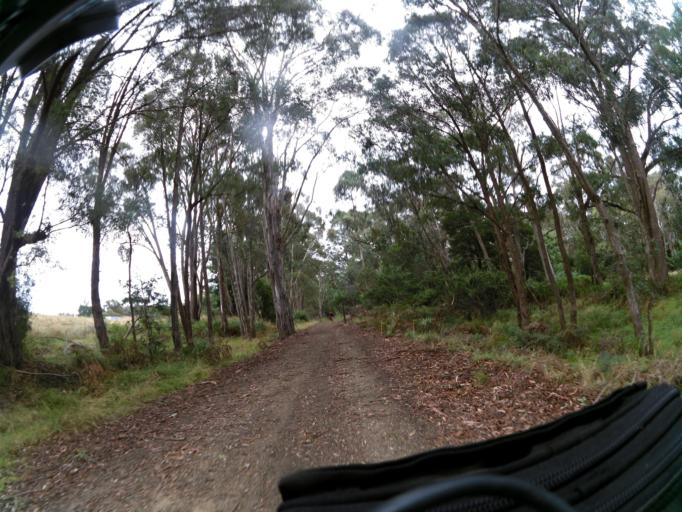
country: AU
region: New South Wales
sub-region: Greater Hume Shire
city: Holbrook
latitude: -36.1512
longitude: 147.4824
